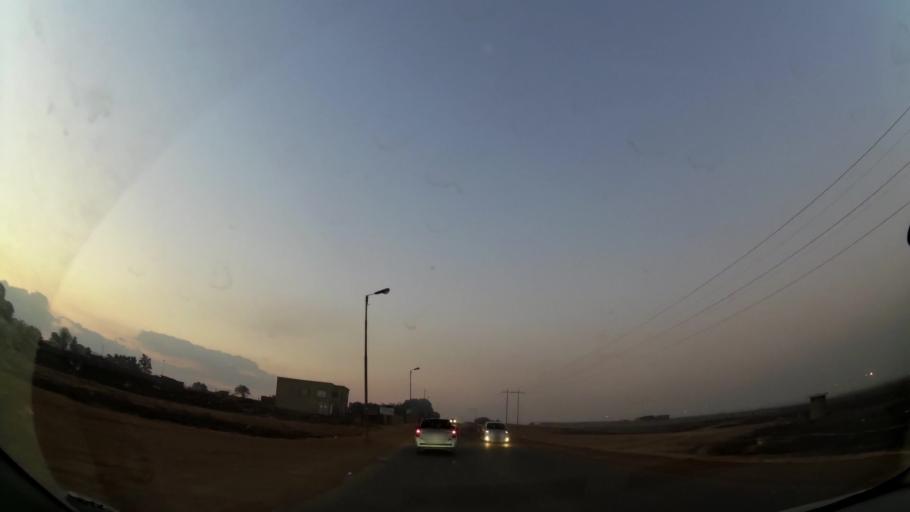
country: ZA
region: Gauteng
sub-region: Ekurhuleni Metropolitan Municipality
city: Springs
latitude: -26.3205
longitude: 28.3763
